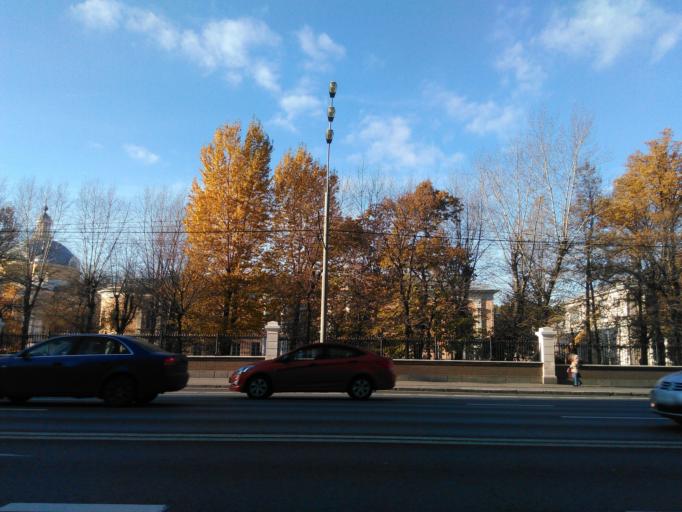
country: RU
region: Moscow
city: Novyye Cheremushki
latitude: 55.7231
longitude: 37.6030
